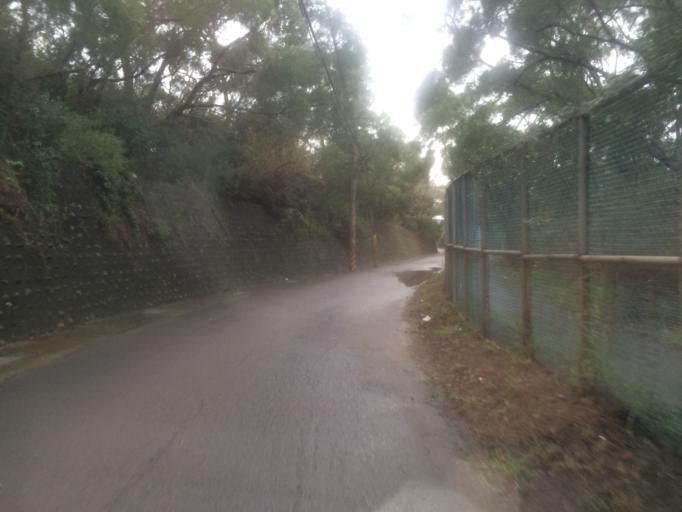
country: TW
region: Taiwan
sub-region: Hsinchu
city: Hsinchu
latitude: 24.7647
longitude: 120.9669
